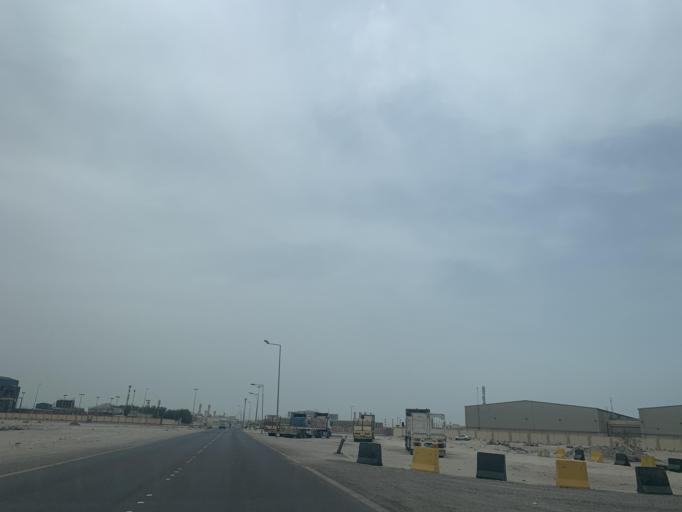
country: BH
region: Muharraq
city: Al Hadd
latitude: 26.2075
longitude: 50.6738
